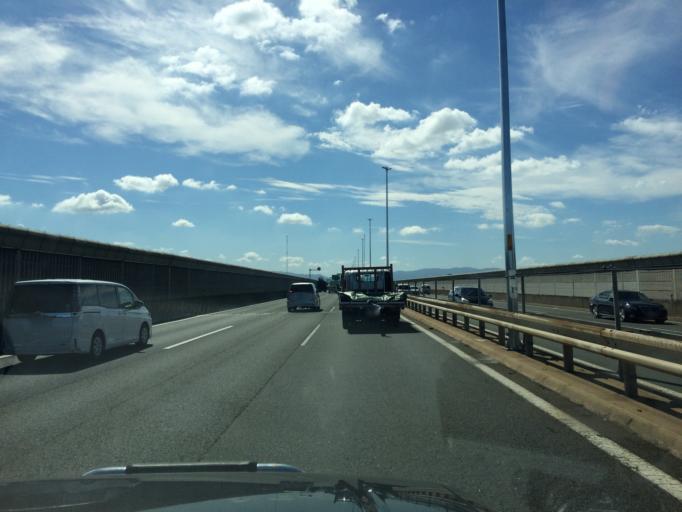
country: JP
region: Osaka
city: Matsubara
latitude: 34.5693
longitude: 135.5643
